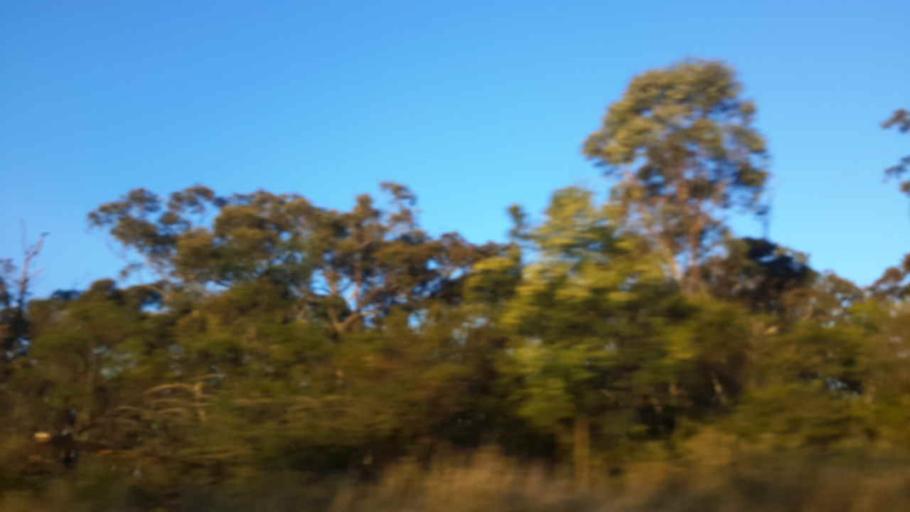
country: AU
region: New South Wales
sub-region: Wollongong
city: Mount Keira
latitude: -34.3413
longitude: 150.7950
